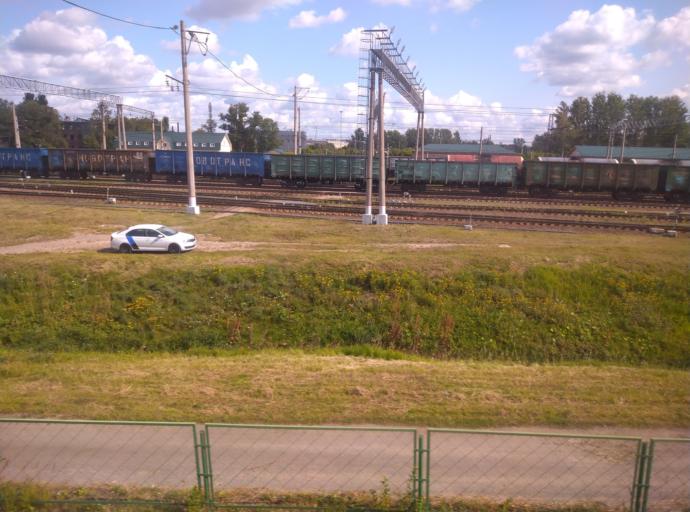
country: RU
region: St.-Petersburg
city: Obukhovo
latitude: 59.8659
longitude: 30.4268
